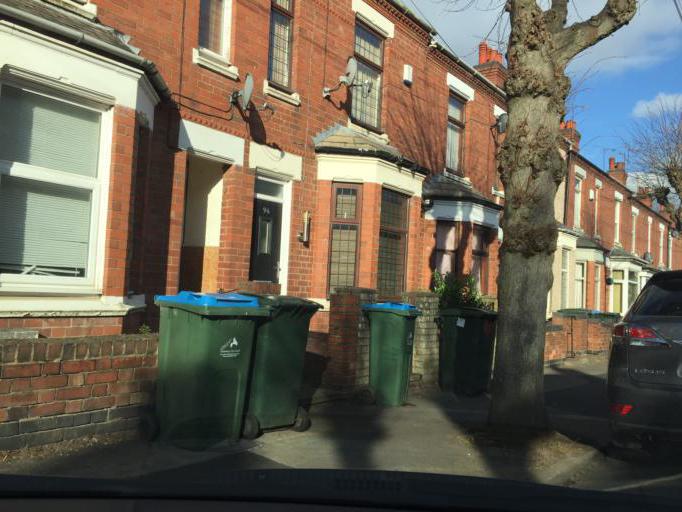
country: GB
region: England
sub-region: Coventry
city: Coventry
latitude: 52.4042
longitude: -1.4855
